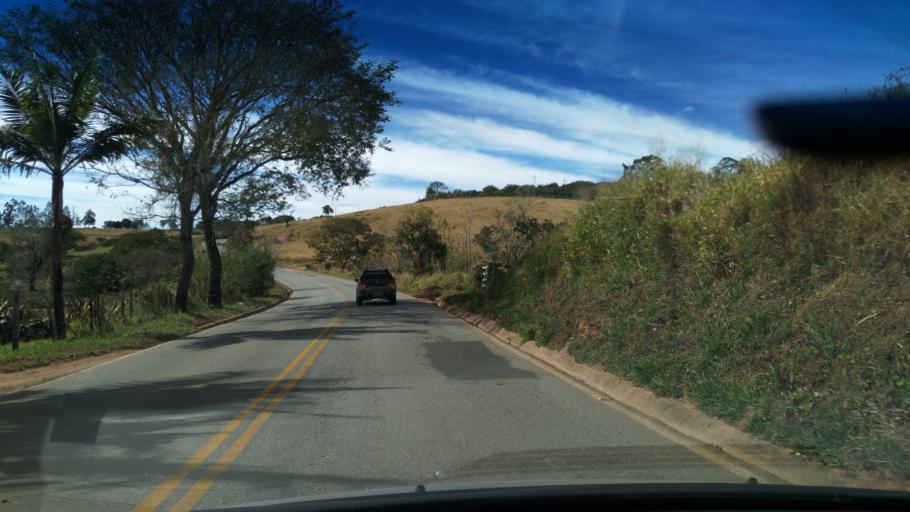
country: BR
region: Minas Gerais
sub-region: Andradas
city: Andradas
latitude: -22.0673
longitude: -46.4592
